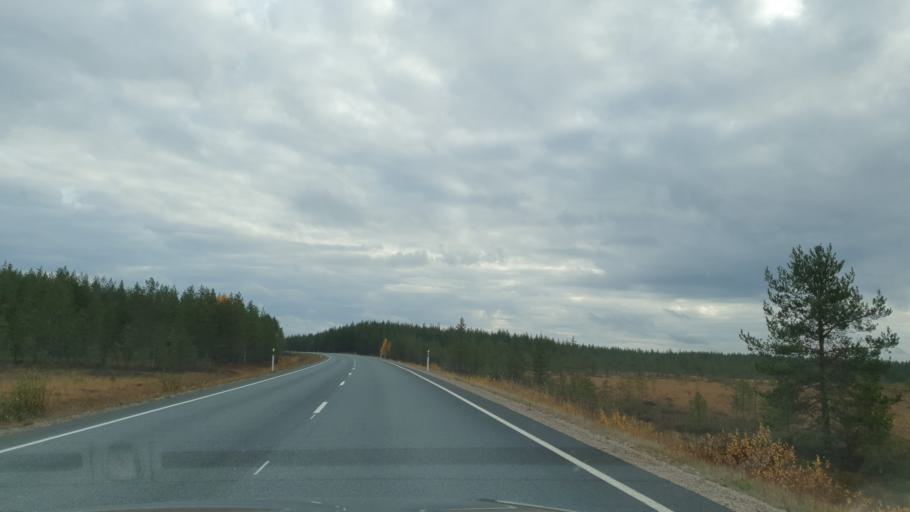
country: FI
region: Northern Ostrobothnia
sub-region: Oulunkaari
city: Pudasjaervi
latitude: 65.4021
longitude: 26.9078
